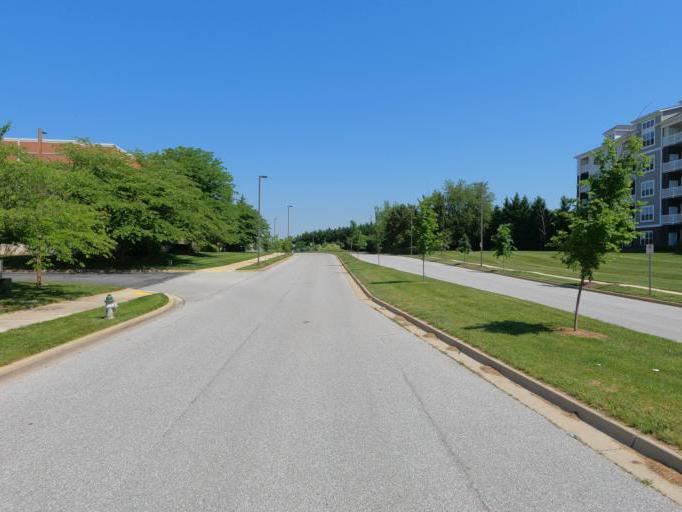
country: US
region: Maryland
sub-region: Montgomery County
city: Germantown
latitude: 39.1928
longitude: -77.2658
